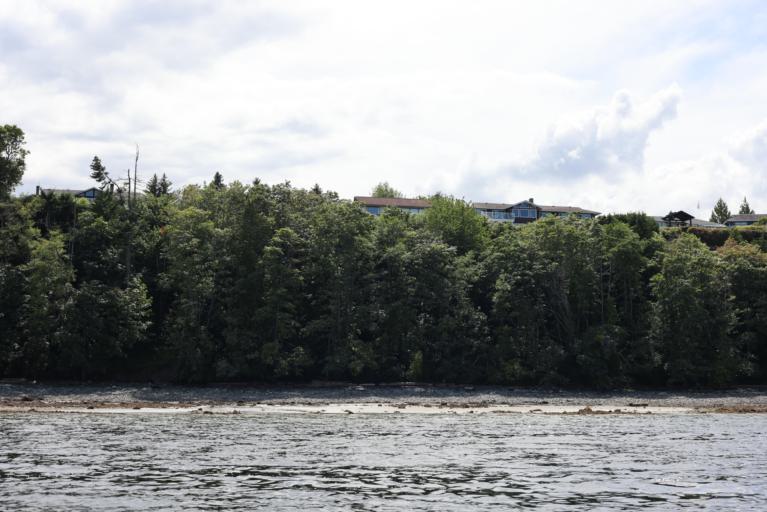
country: CA
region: British Columbia
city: Nanaimo
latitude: 49.1980
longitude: -123.9632
